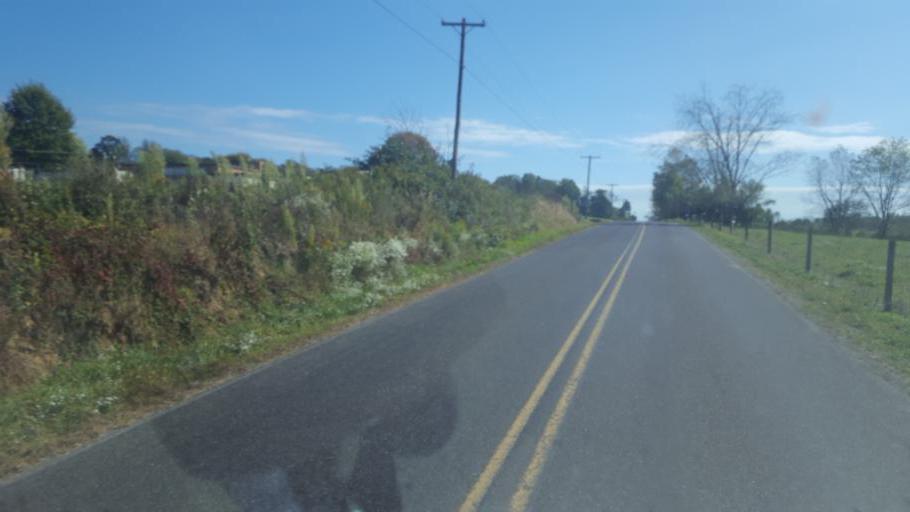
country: US
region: Pennsylvania
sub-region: Mercer County
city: Greenville
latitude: 41.4022
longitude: -80.4508
